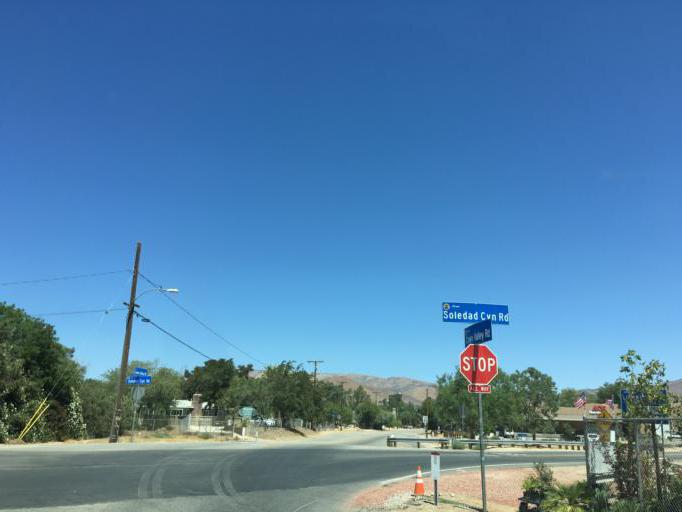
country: US
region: California
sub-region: Los Angeles County
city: Acton
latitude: 34.4657
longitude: -118.1970
